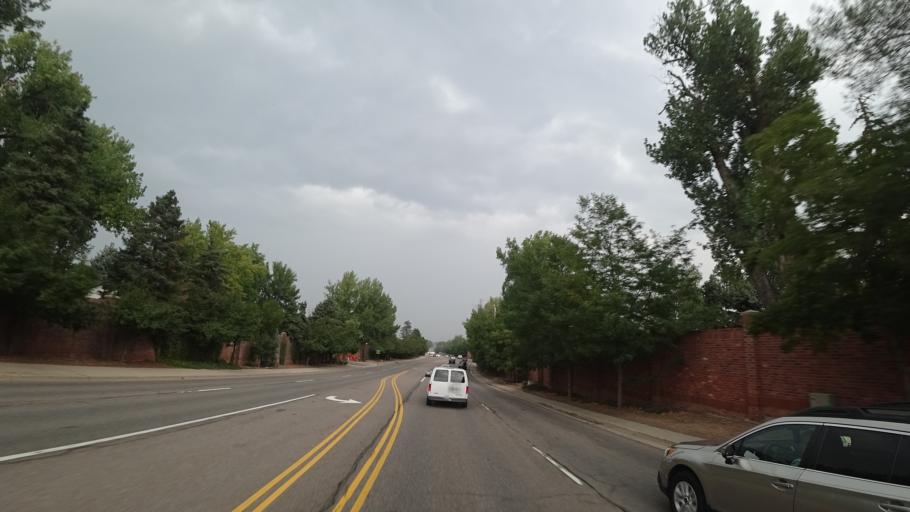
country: US
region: Colorado
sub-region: Arapahoe County
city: Greenwood Village
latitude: 39.6152
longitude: -104.9599
